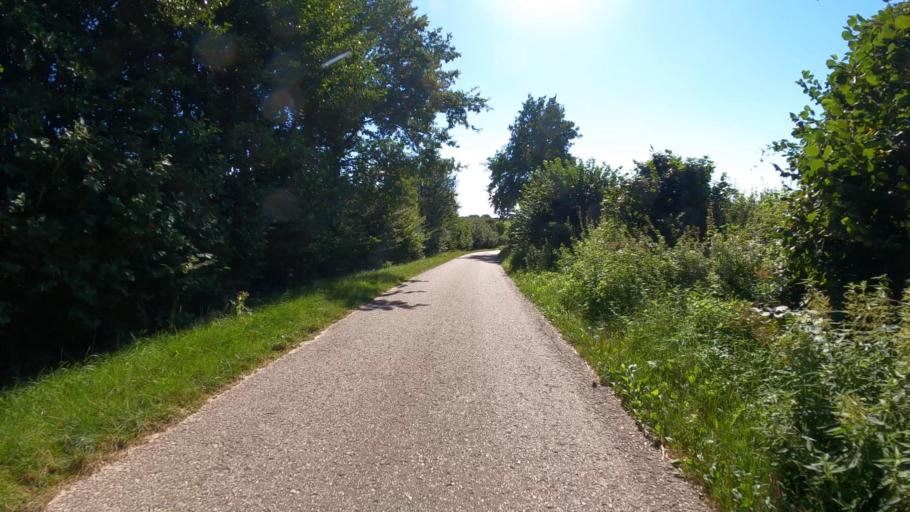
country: DE
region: Schleswig-Holstein
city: Gross Schenkenberg
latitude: 53.8017
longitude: 10.5677
